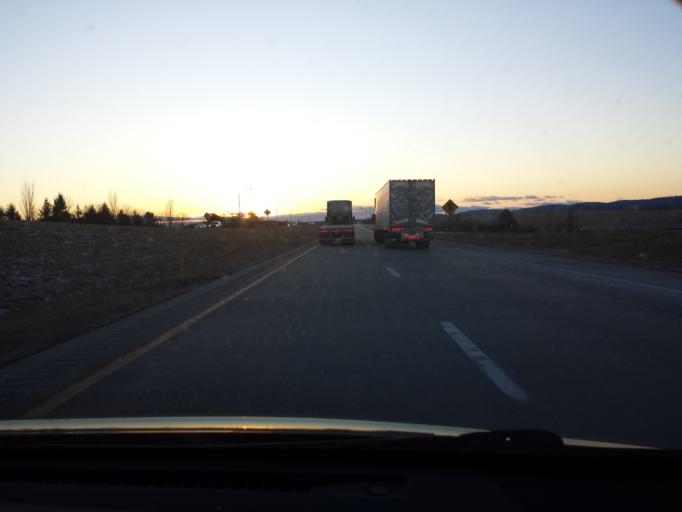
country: US
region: Pennsylvania
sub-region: Centre County
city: Pleasant Gap
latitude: 40.8842
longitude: -77.7420
